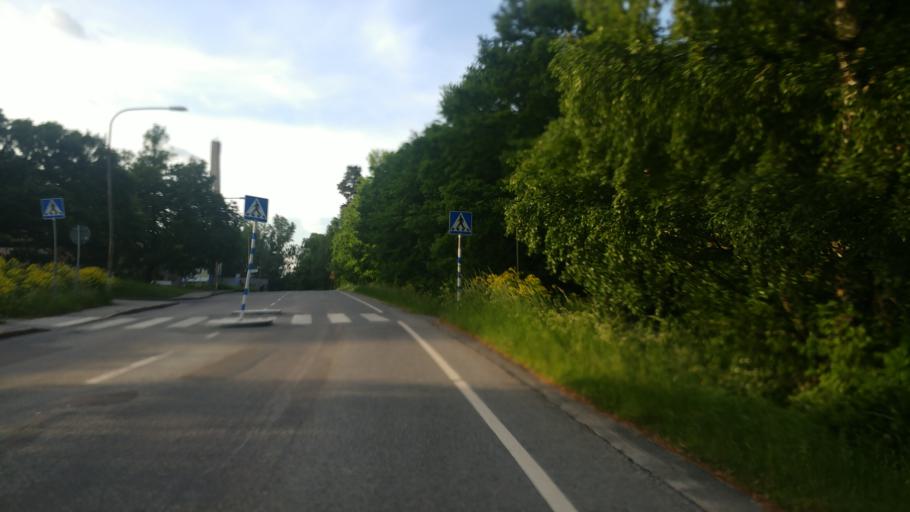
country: SE
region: Stockholm
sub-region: Danderyds Kommun
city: Djursholm
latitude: 59.3698
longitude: 18.0676
